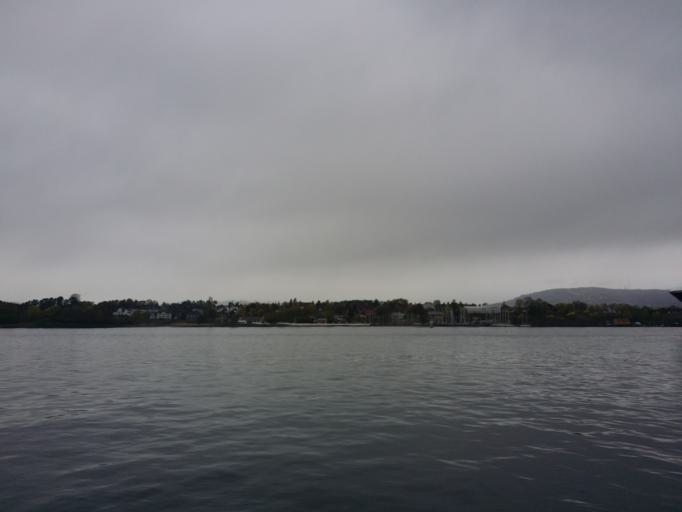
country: NO
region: Oslo
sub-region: Oslo
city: Sjolyststranda
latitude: 59.8950
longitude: 10.7001
